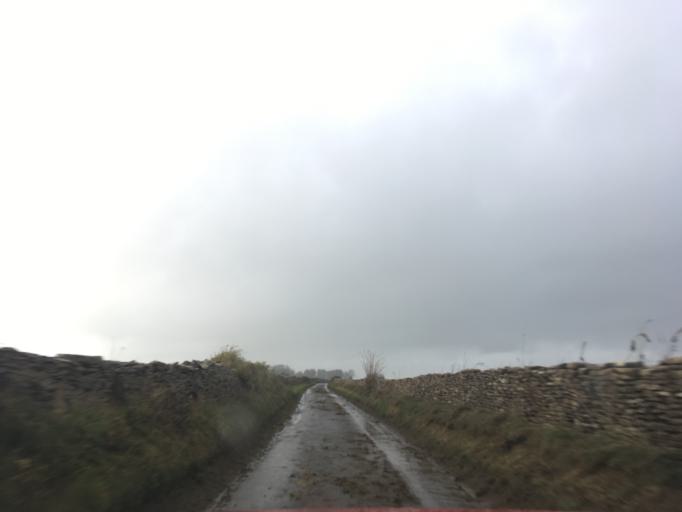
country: GB
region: England
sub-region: South Gloucestershire
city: Cold Ashton
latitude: 51.4679
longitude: -2.3525
